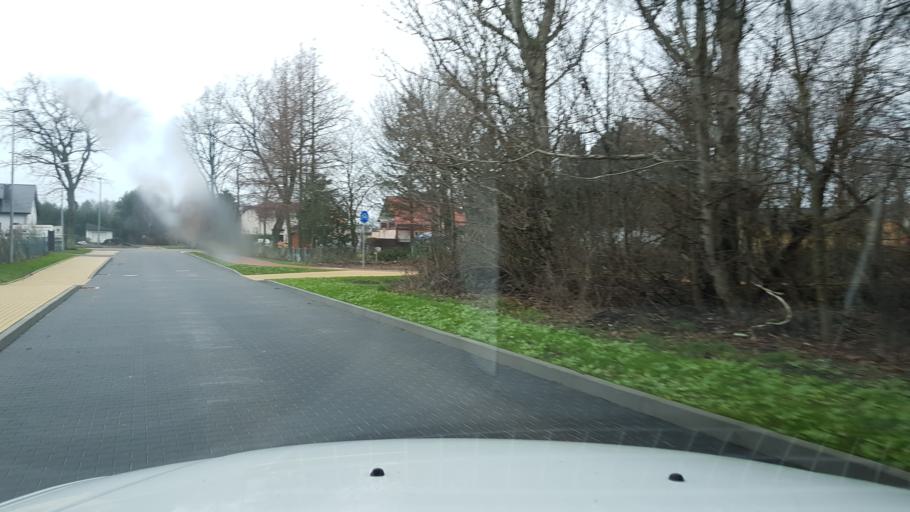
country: PL
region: West Pomeranian Voivodeship
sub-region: Powiat kolobrzeski
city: Grzybowo
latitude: 54.1585
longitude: 15.4938
